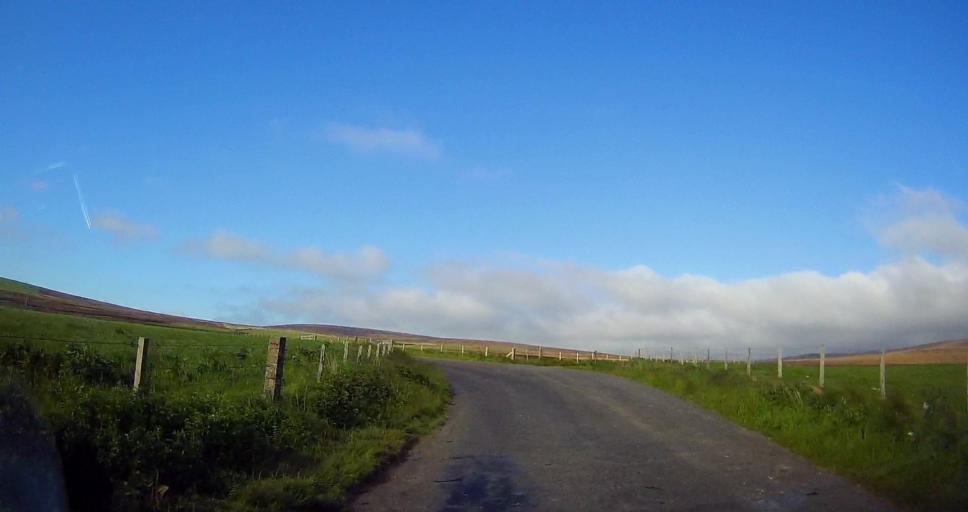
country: GB
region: Scotland
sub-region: Orkney Islands
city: Stromness
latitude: 59.0876
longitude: -3.1836
